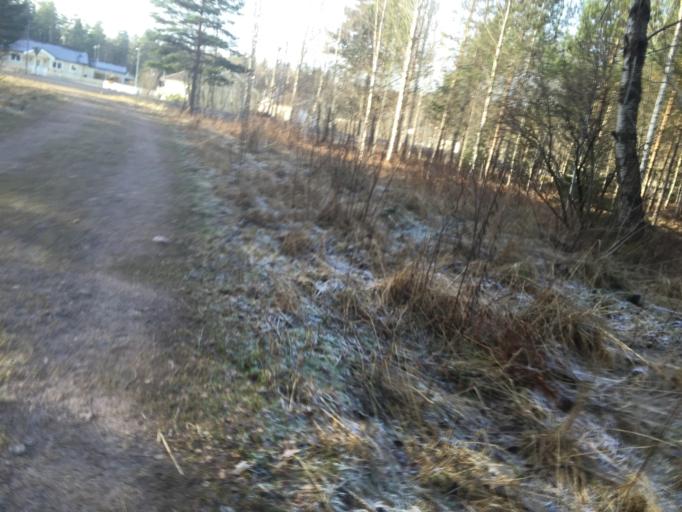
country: SE
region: Joenkoeping
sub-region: Aneby Kommun
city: Aneby
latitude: 57.8473
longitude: 14.7974
